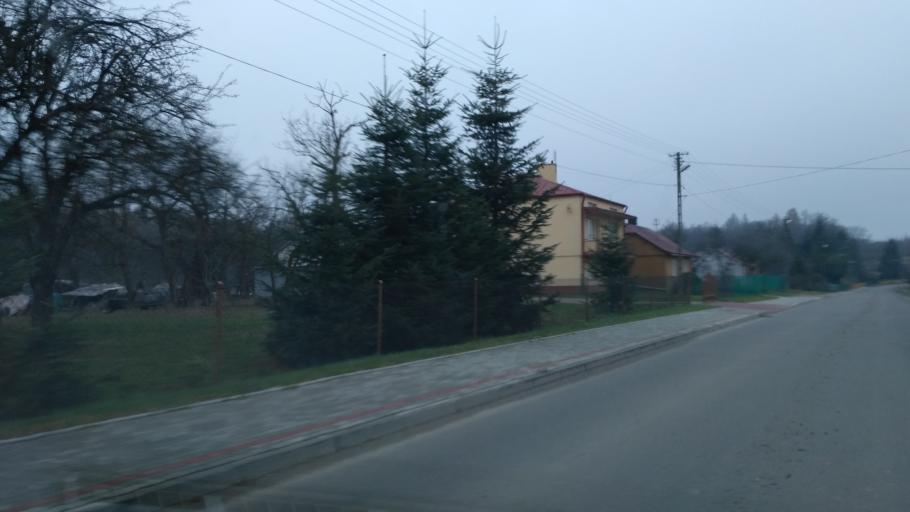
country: PL
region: Subcarpathian Voivodeship
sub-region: Powiat jaroslawski
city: Pawlosiow
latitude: 49.9813
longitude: 22.6354
